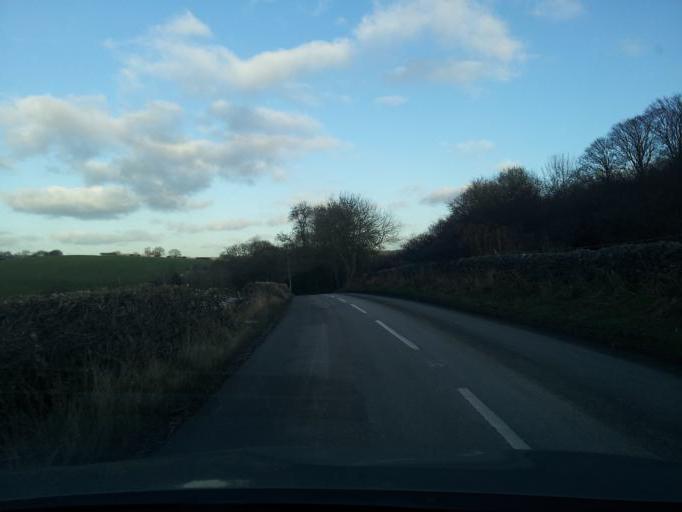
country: GB
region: England
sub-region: Derbyshire
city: Matlock
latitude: 53.1436
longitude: -1.6217
